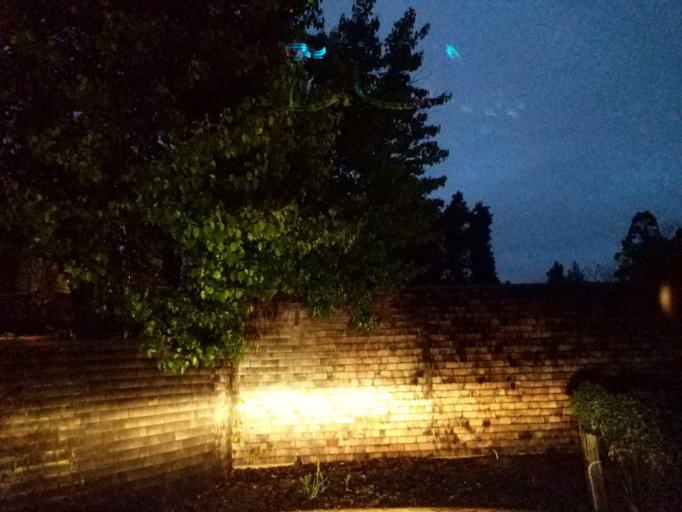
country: US
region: California
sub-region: Santa Clara County
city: Los Altos Hills
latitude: 37.3944
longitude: -122.1328
